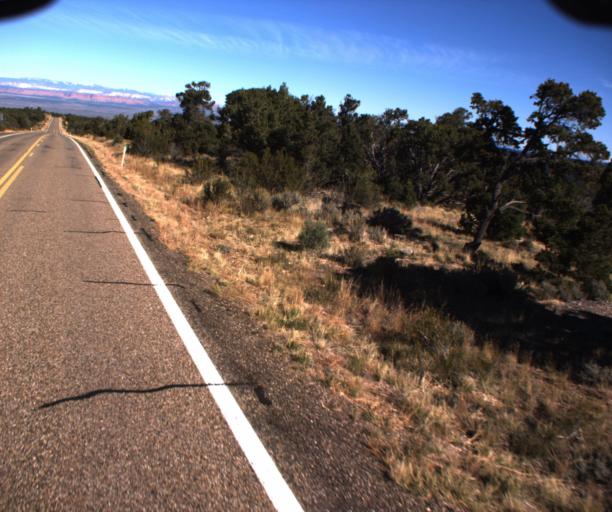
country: US
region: Arizona
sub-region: Coconino County
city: Fredonia
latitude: 36.8172
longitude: -112.2528
